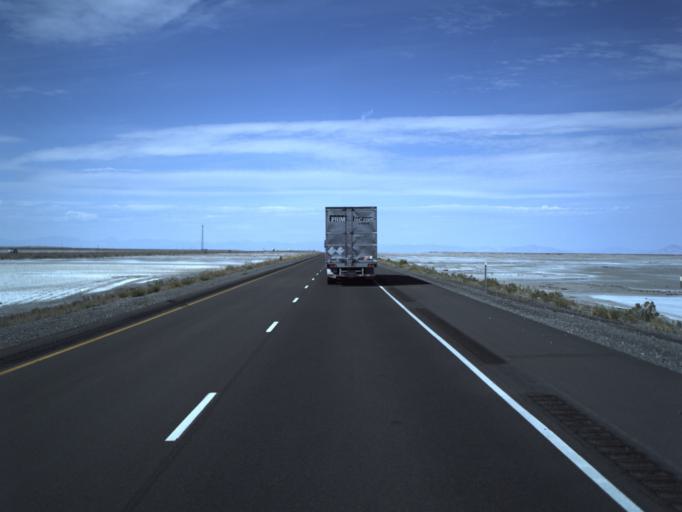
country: US
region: Utah
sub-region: Tooele County
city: Wendover
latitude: 40.7281
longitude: -113.2994
